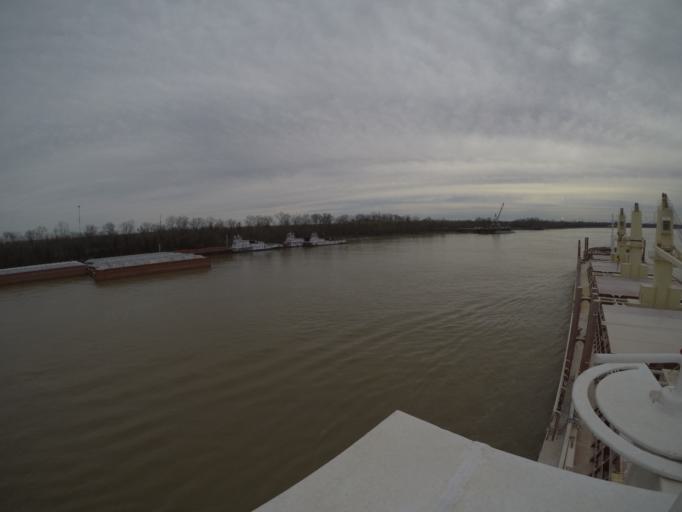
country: US
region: Louisiana
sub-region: Saint John the Baptist Parish
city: Laplace
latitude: 30.0427
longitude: -90.4746
